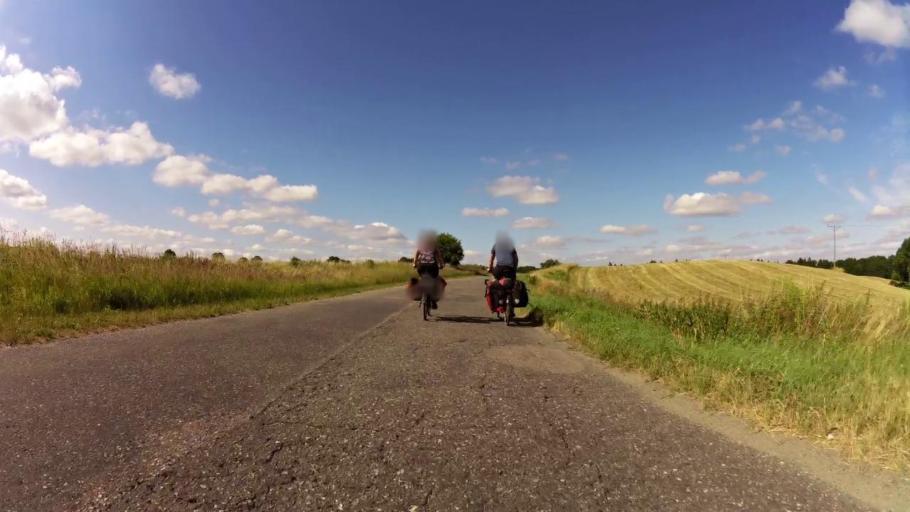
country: PL
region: West Pomeranian Voivodeship
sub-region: Powiat lobeski
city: Lobez
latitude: 53.6475
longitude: 15.6732
